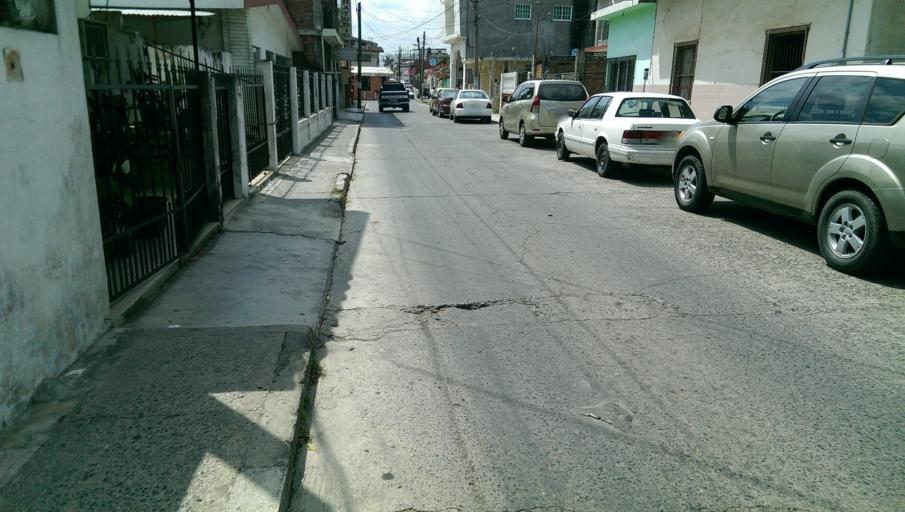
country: MX
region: Veracruz
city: Tuxpan de Rodriguez Cano
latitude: 20.9574
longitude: -97.4088
